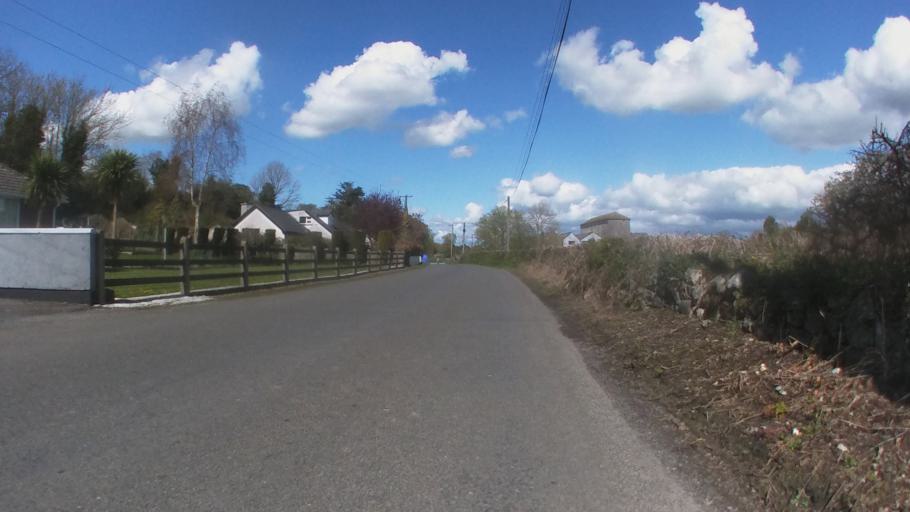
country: IE
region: Leinster
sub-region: Kilkenny
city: Thomastown
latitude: 52.5882
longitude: -7.1857
